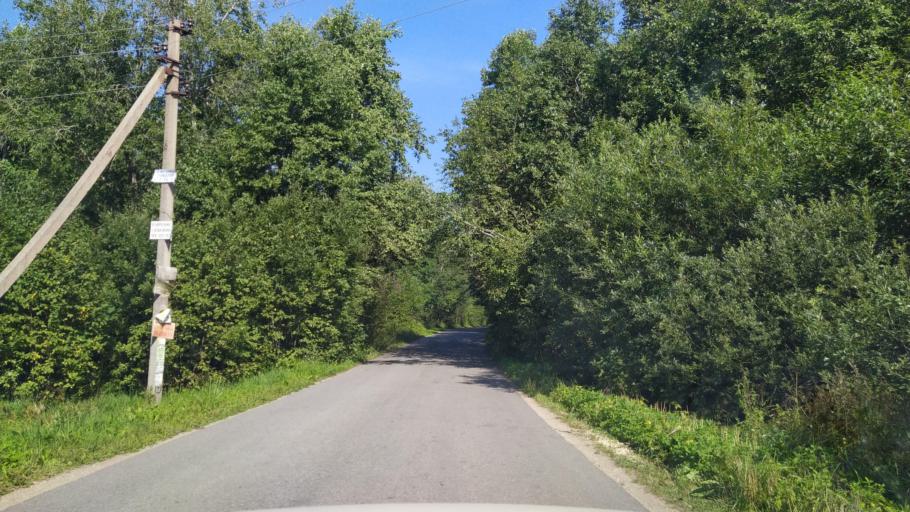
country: RU
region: Leningrad
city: Rozhdestveno
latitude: 59.2663
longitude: 30.0237
